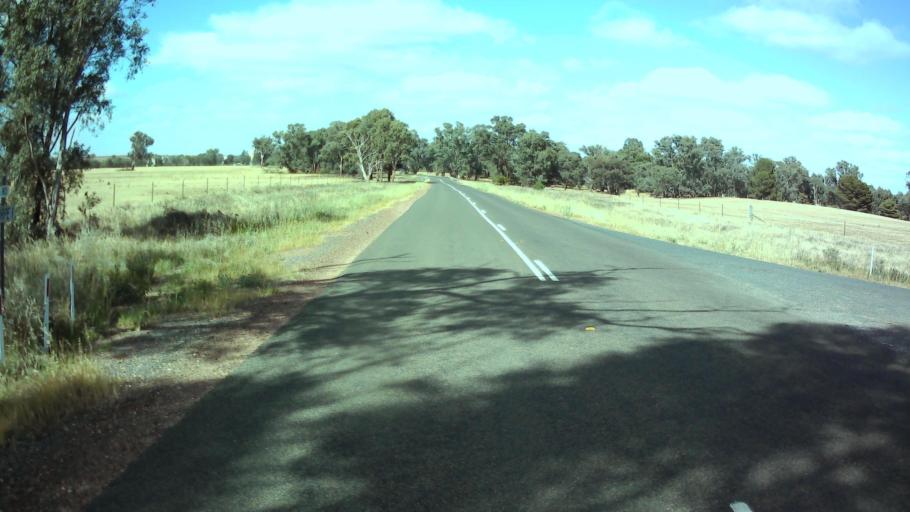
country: AU
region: New South Wales
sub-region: Weddin
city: Grenfell
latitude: -33.9874
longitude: 148.4119
